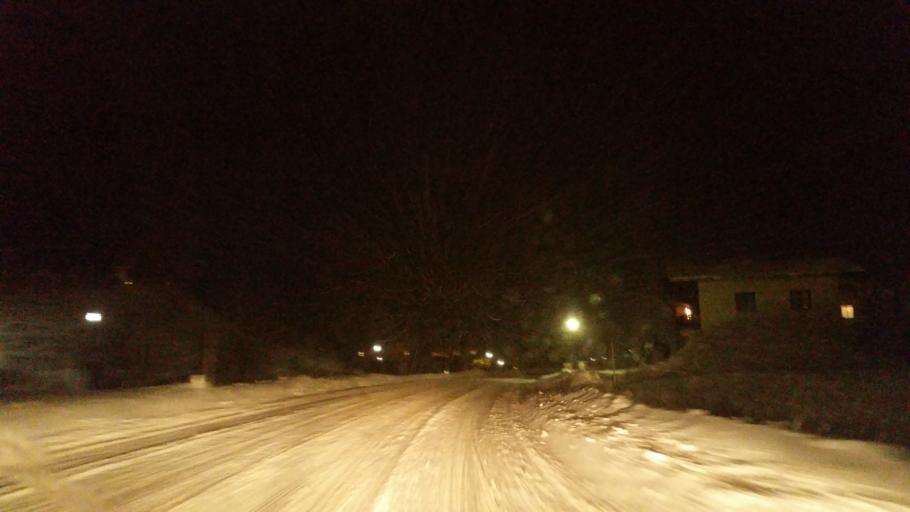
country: AT
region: Salzburg
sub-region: Politischer Bezirk Hallein
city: Abtenau
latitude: 47.5195
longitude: 13.4305
